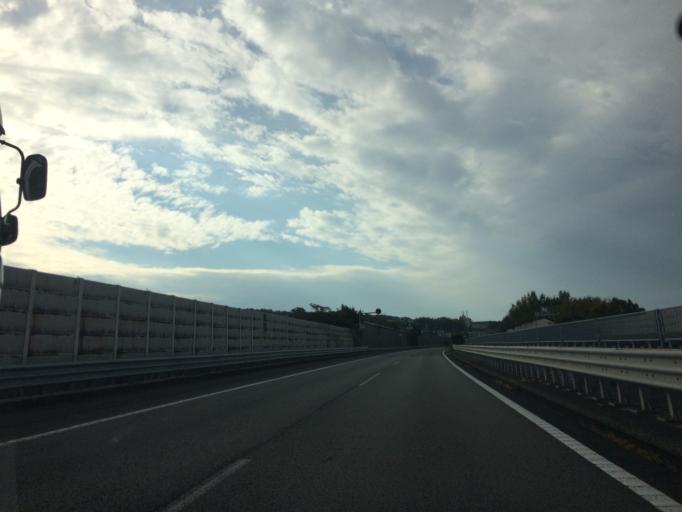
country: JP
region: Shizuoka
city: Shizuoka-shi
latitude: 34.9936
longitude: 138.4352
